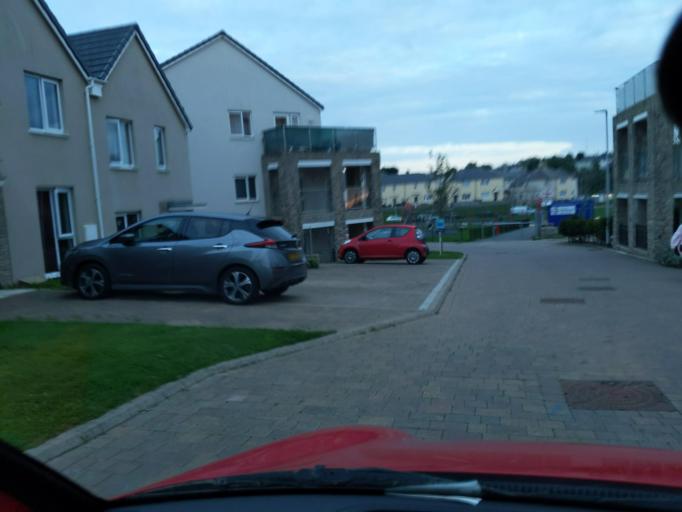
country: GB
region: England
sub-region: Cornwall
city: Millbrook
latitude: 50.3928
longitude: -4.1713
